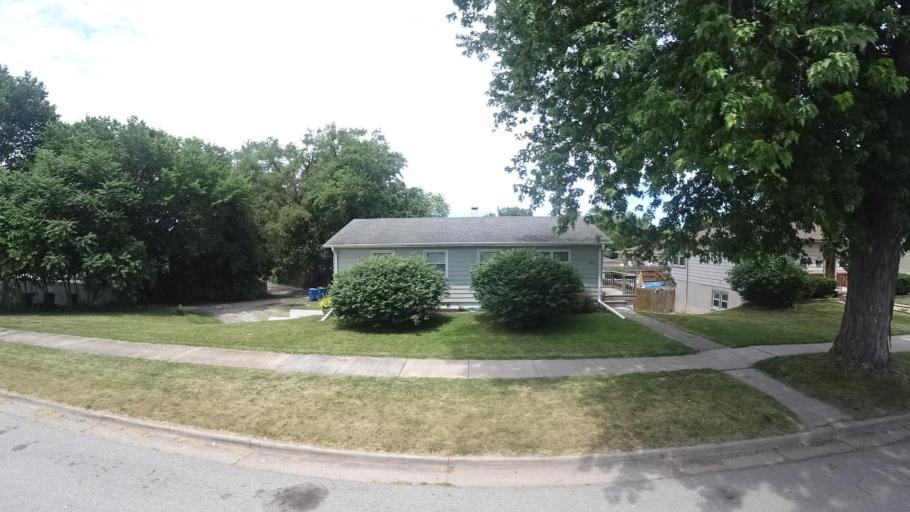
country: US
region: Indiana
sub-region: Porter County
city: Porter
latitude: 41.6178
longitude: -87.0761
